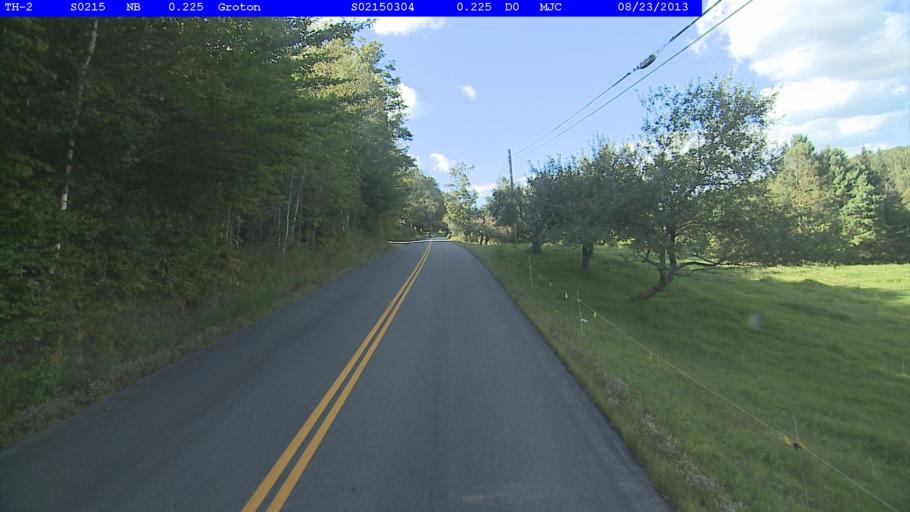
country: US
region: New Hampshire
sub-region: Grafton County
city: Woodsville
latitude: 44.2122
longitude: -72.1910
